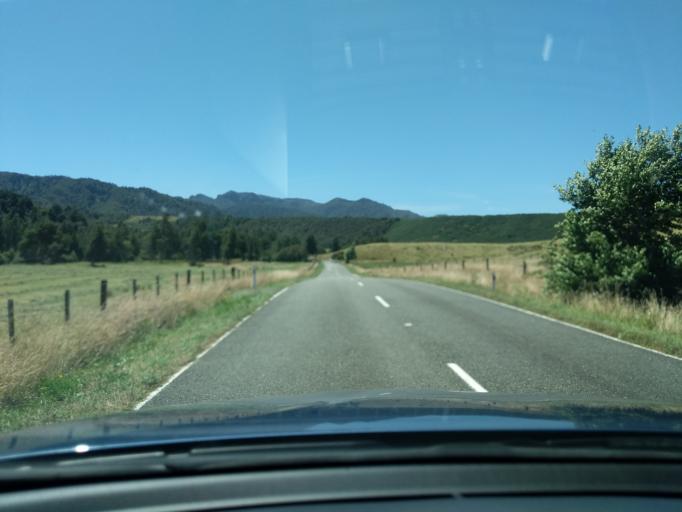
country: NZ
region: Tasman
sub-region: Tasman District
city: Takaka
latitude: -40.7444
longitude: 172.5669
